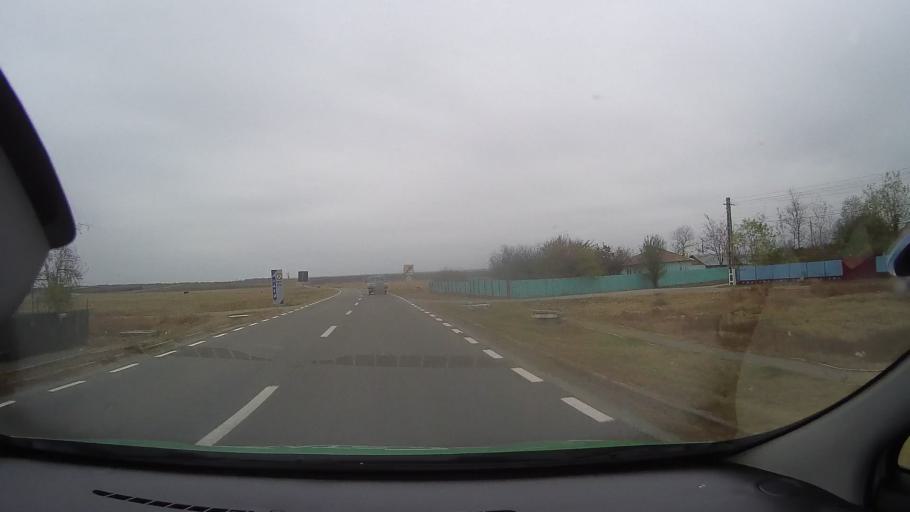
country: RO
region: Ialomita
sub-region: Comuna Scanteia
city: Iazu
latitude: 44.7269
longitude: 27.4240
